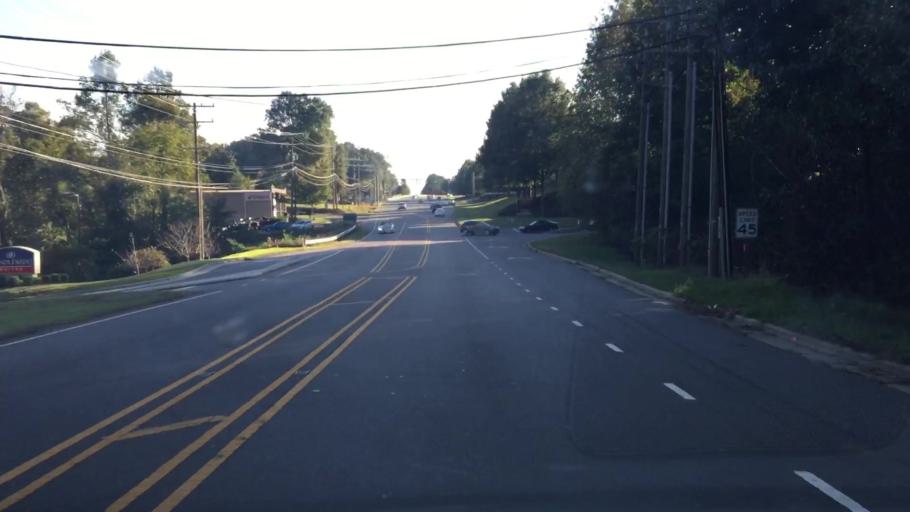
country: US
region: North Carolina
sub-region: Iredell County
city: Mooresville
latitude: 35.5572
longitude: -80.8528
